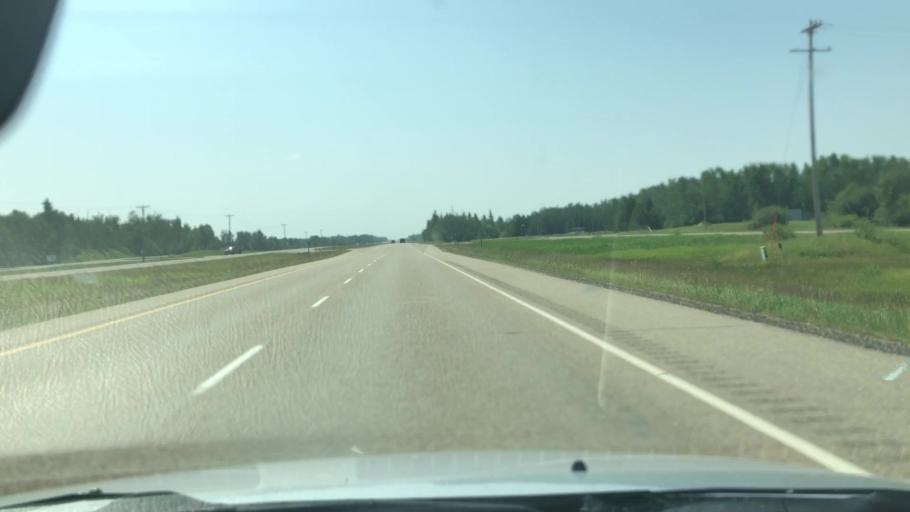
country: CA
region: Alberta
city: Devon
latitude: 53.4377
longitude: -113.7630
